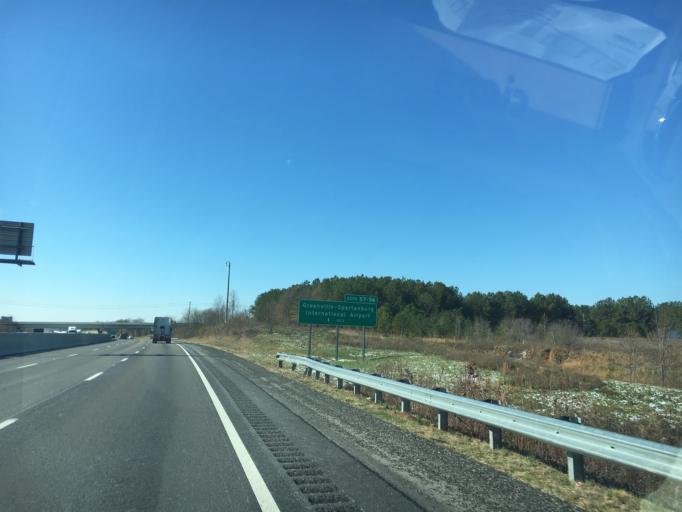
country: US
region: South Carolina
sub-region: Greenville County
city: Greer
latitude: 34.8860
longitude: -82.1917
